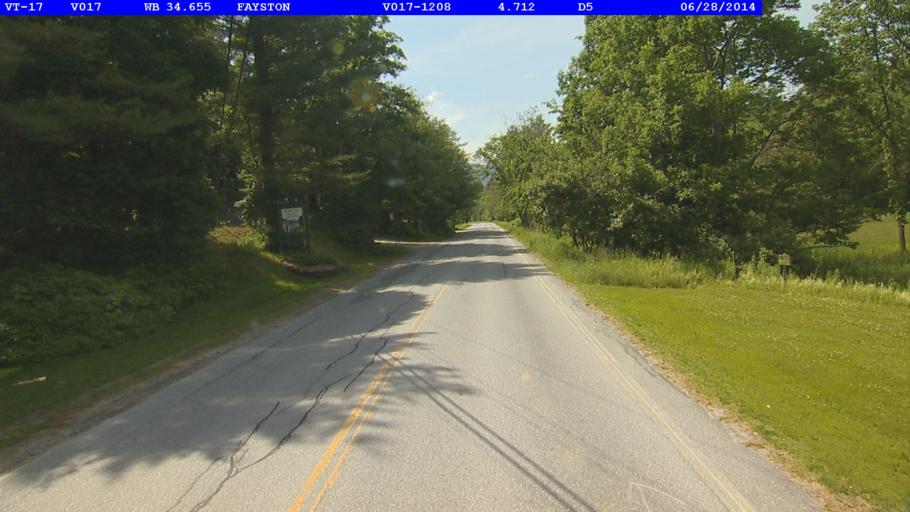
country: US
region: Vermont
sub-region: Washington County
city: Waterbury
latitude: 44.1822
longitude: -72.8647
